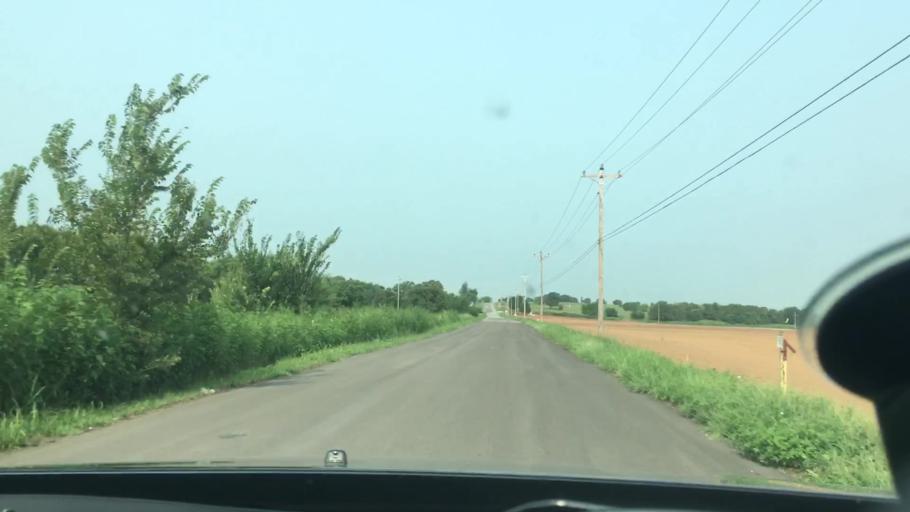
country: US
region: Oklahoma
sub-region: Garvin County
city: Lindsay
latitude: 34.8121
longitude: -97.6274
